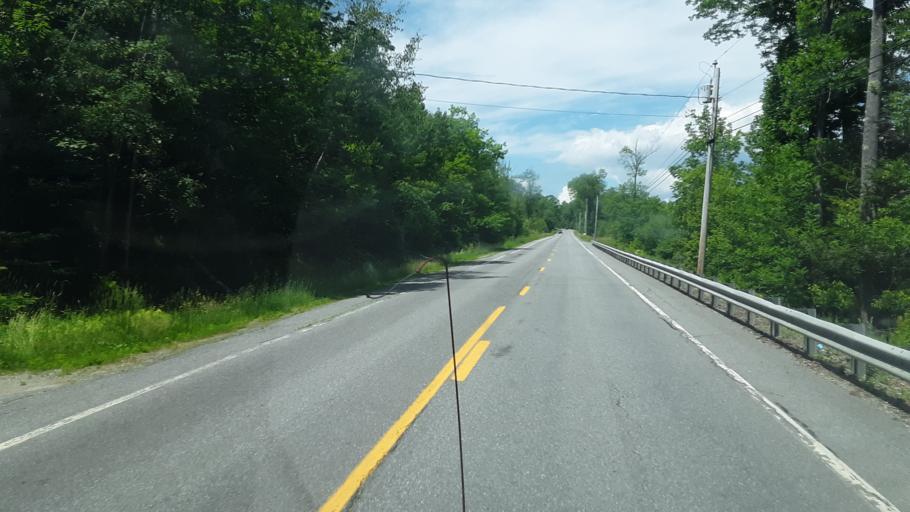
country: US
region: Maine
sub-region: Hancock County
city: Bucksport
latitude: 44.5696
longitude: -68.8123
